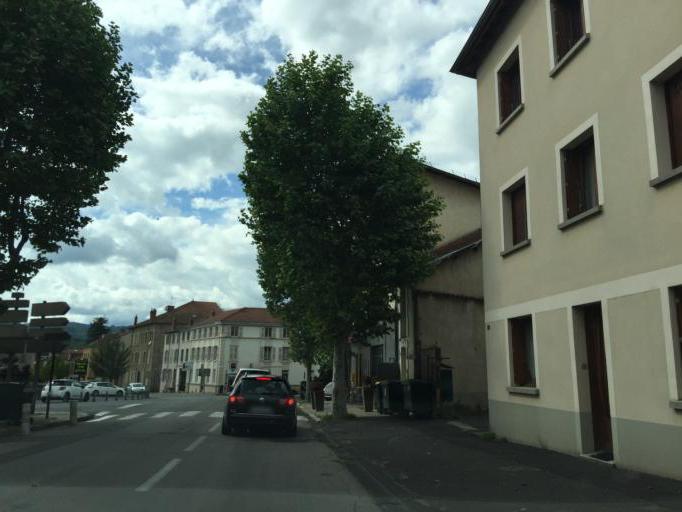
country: FR
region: Auvergne
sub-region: Departement du Puy-de-Dome
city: Ambert
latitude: 45.5484
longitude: 3.7457
